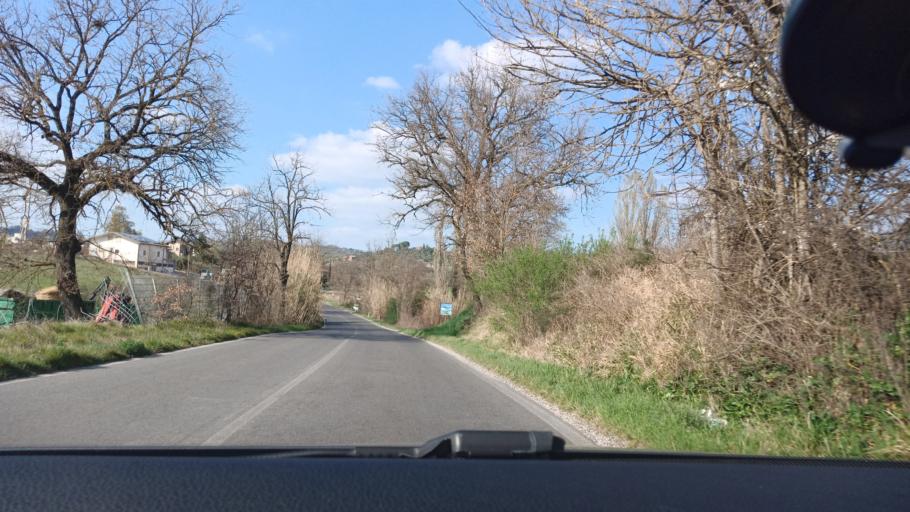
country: IT
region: Latium
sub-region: Citta metropolitana di Roma Capitale
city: Torrita Tiberina
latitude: 42.2575
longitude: 12.6394
